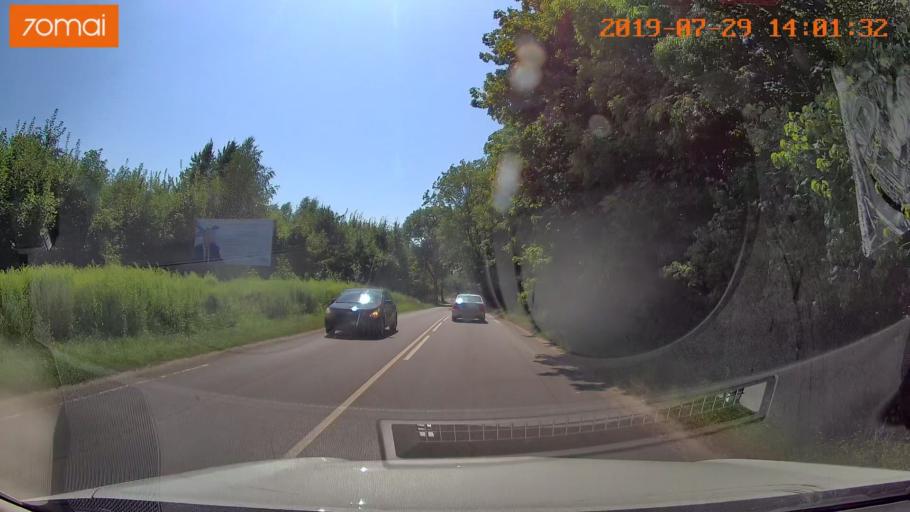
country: RU
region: Kaliningrad
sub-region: Gorod Kaliningrad
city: Baltiysk
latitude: 54.6698
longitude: 19.9209
